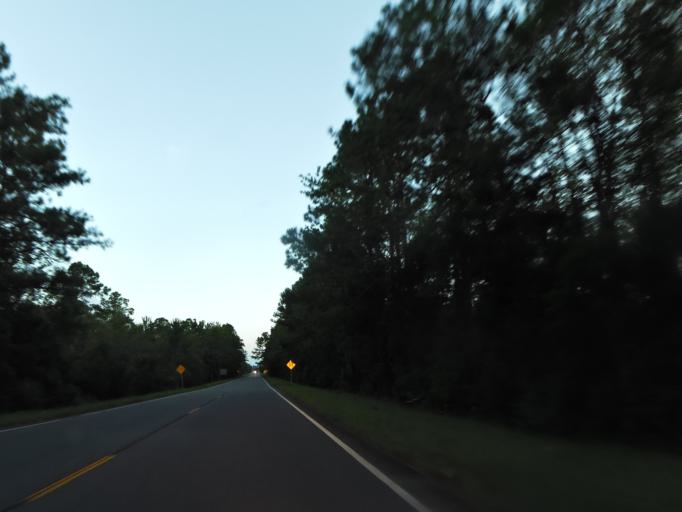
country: US
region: Georgia
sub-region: Camden County
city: Kingsland
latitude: 30.7467
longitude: -81.6875
